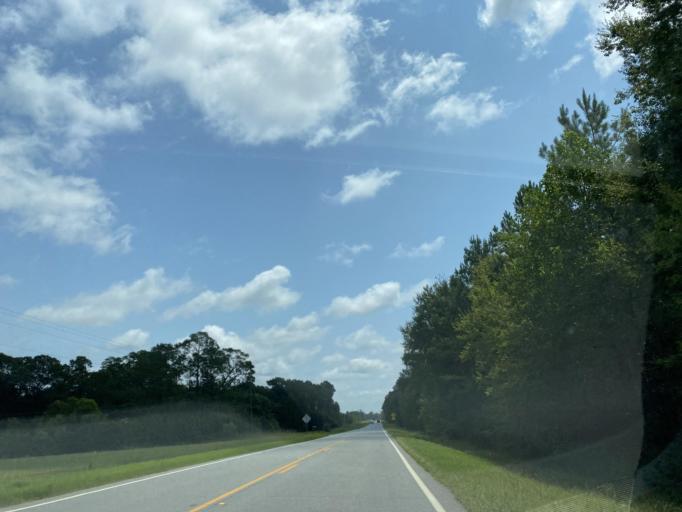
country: US
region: Georgia
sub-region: Telfair County
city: Helena
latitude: 32.0297
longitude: -83.0258
